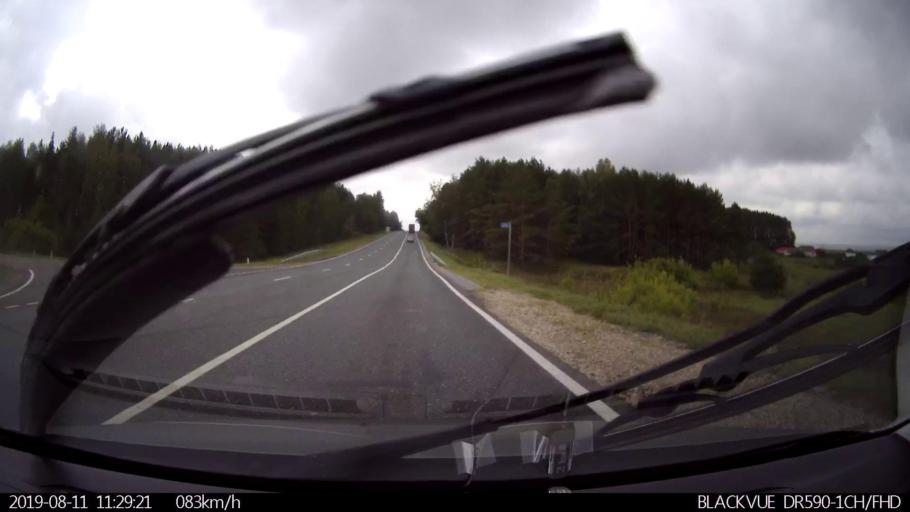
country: RU
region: Ulyanovsk
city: Krasnyy Gulyay
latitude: 54.0711
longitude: 48.2239
